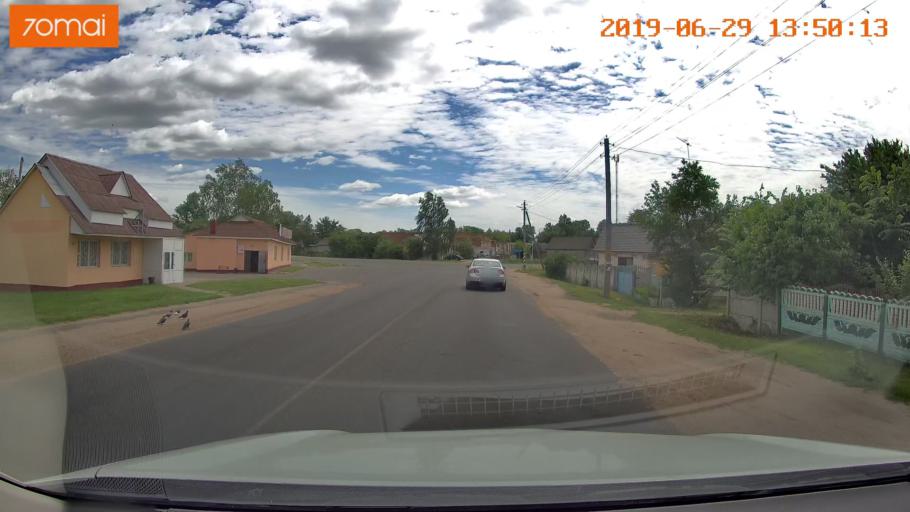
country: BY
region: Minsk
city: Slutsk
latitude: 53.0040
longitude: 27.5671
